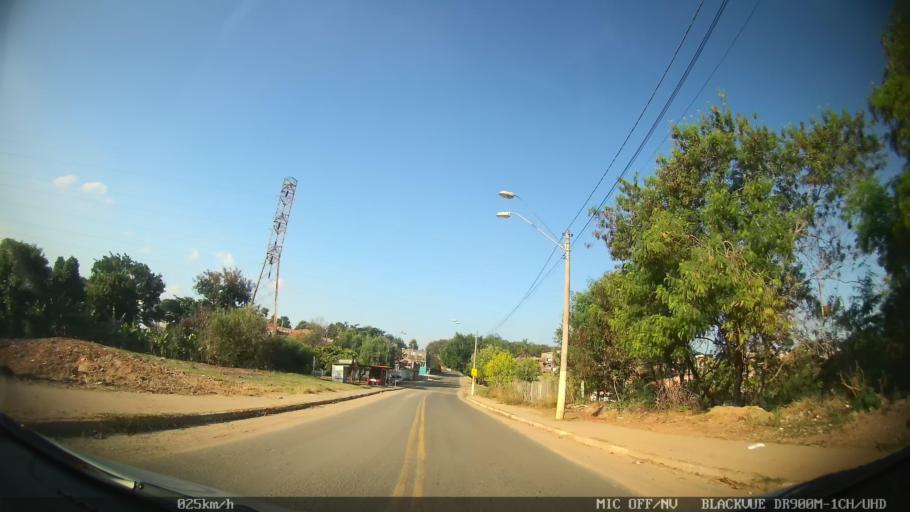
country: BR
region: Sao Paulo
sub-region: Campinas
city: Campinas
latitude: -22.9712
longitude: -47.1187
